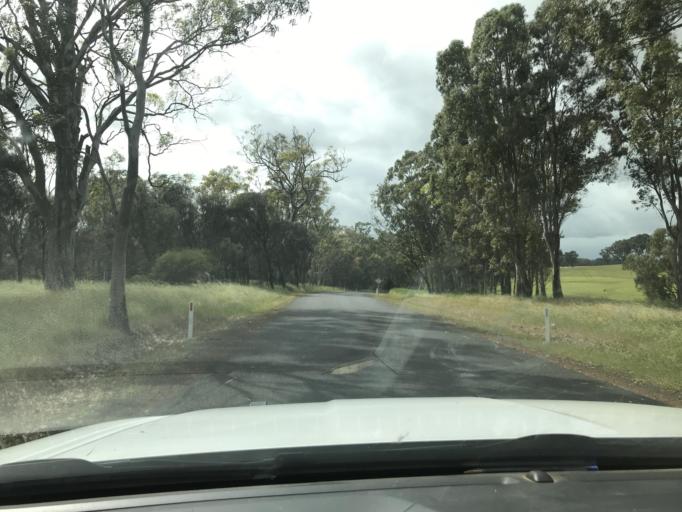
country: AU
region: South Australia
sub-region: Wattle Range
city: Penola
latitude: -37.1692
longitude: 141.4267
